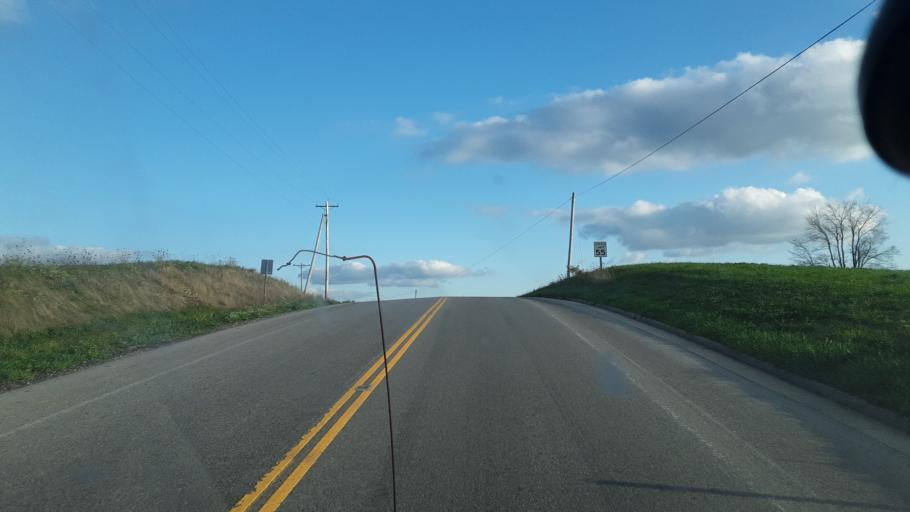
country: US
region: Ohio
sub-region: Tuscarawas County
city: Sugarcreek
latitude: 40.4397
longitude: -81.7623
